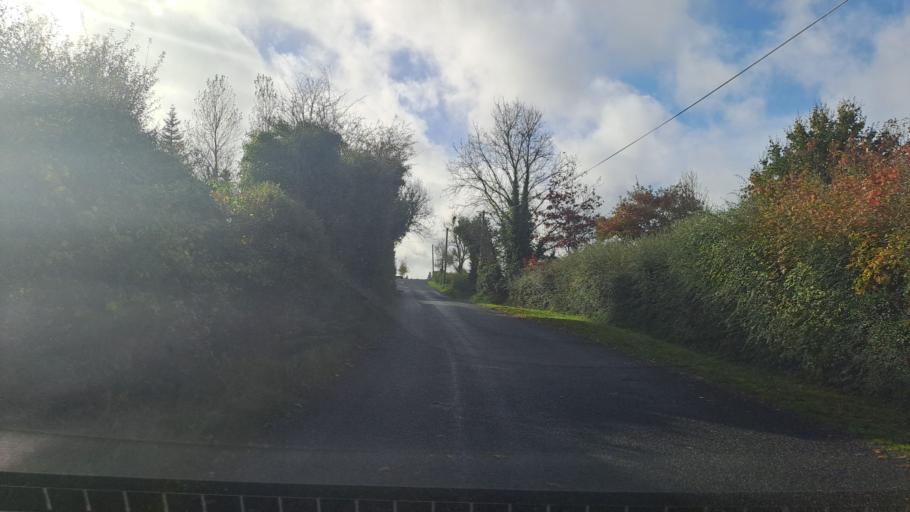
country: IE
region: Ulster
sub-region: An Cabhan
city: Cootehill
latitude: 54.0332
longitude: -7.0165
